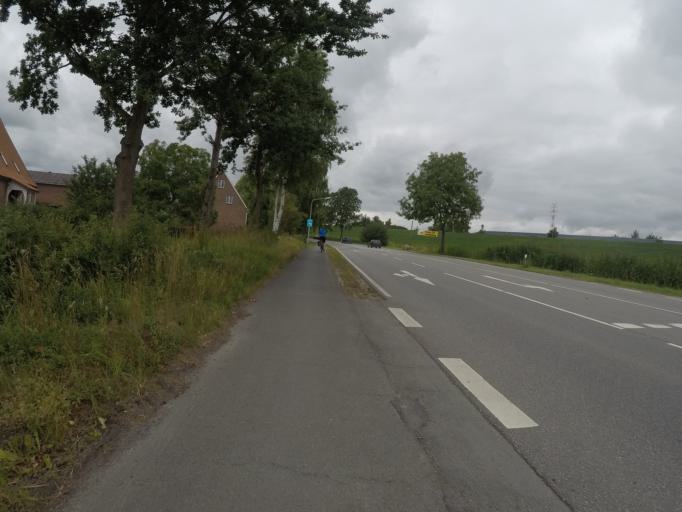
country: DE
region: Lower Saxony
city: Grunendeich
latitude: 53.5798
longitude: 9.6010
